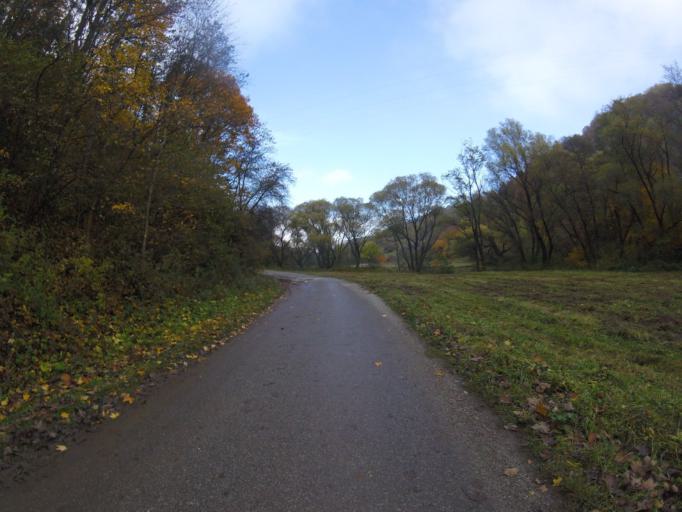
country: HU
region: Borsod-Abauj-Zemplen
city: Putnok
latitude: 48.2141
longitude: 20.4440
